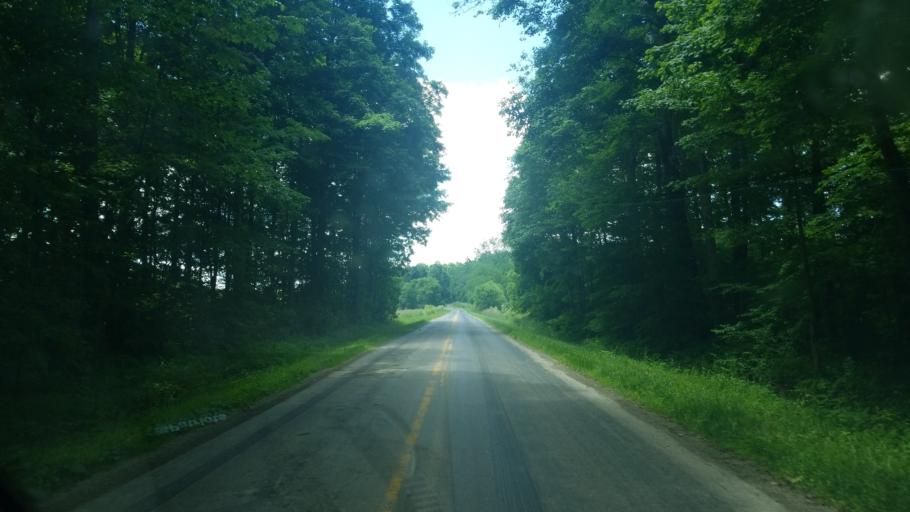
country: US
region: Ohio
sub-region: Huron County
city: New London
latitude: 40.9676
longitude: -82.3875
